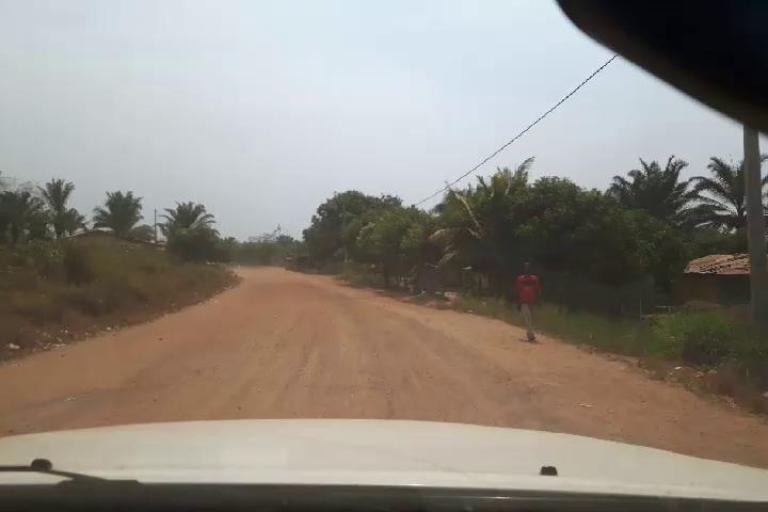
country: SL
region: Northern Province
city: Bumbuna
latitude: 9.0407
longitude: -11.7558
